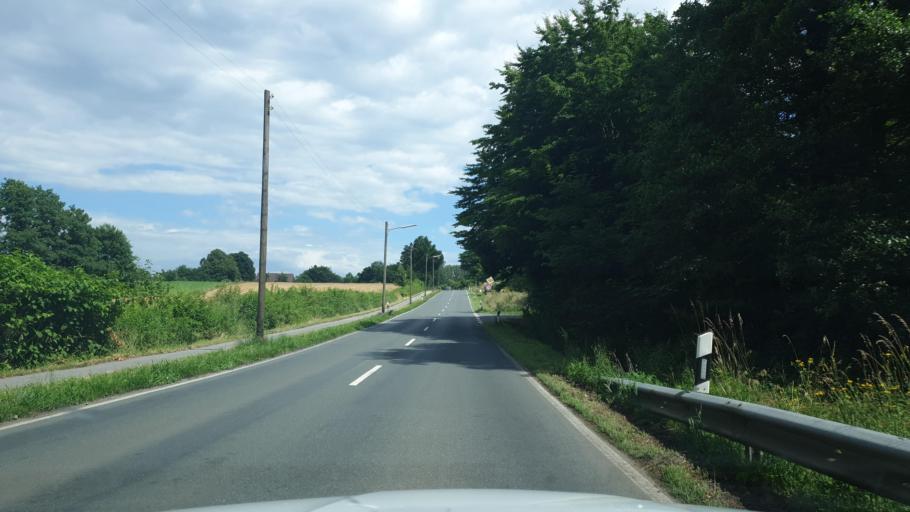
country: DE
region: North Rhine-Westphalia
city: Bad Oeynhausen
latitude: 52.1775
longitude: 8.7821
